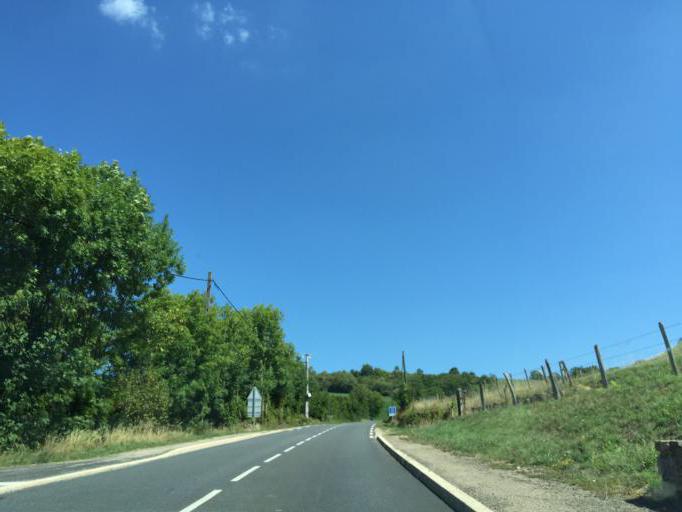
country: FR
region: Midi-Pyrenees
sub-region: Departement de l'Aveyron
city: Espalion
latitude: 44.5321
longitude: 2.7662
